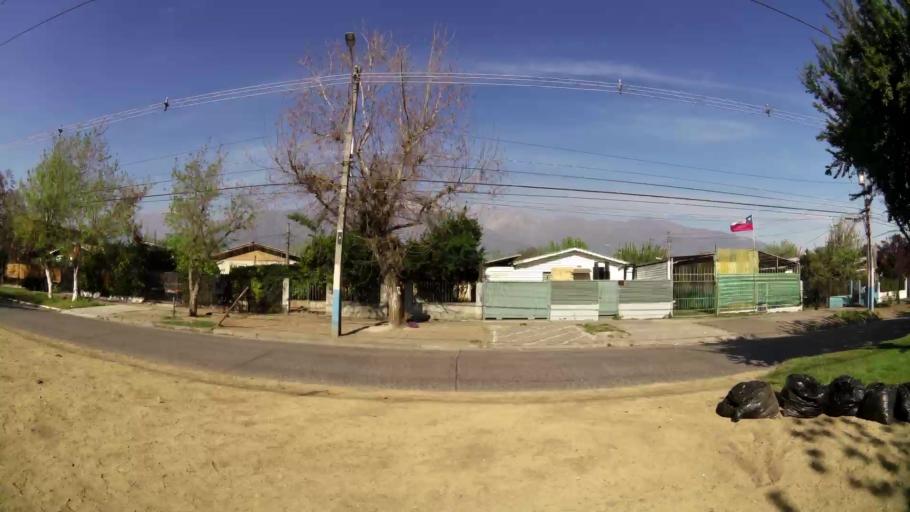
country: CL
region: Santiago Metropolitan
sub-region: Provincia de Santiago
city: Villa Presidente Frei, Nunoa, Santiago, Chile
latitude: -33.4638
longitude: -70.5661
